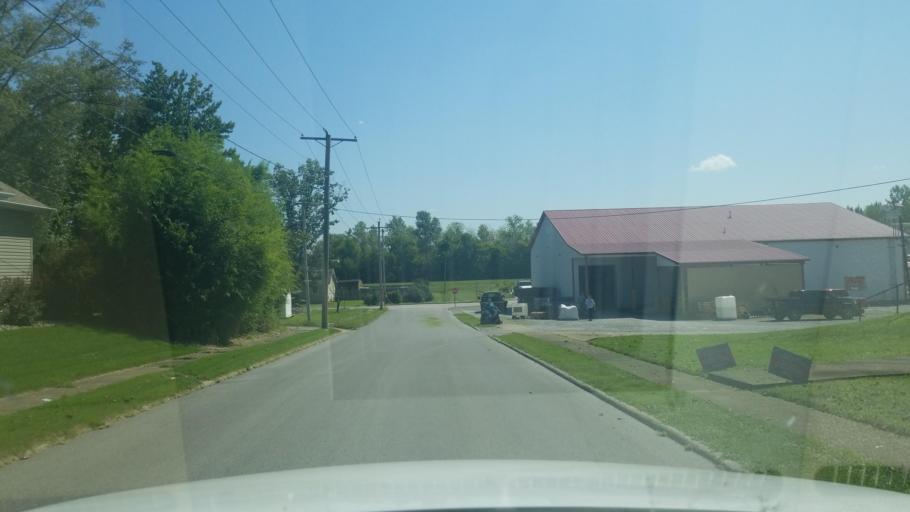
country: US
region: Illinois
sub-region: Saline County
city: Harrisburg
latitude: 37.7239
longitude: -88.5414
